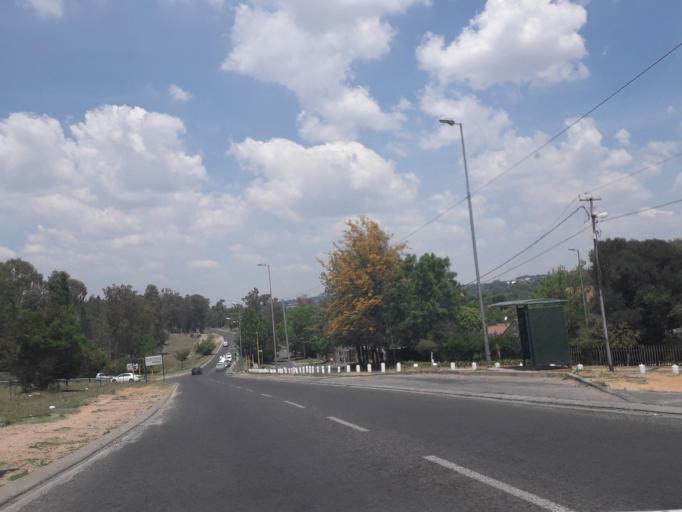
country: ZA
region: Gauteng
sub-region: City of Johannesburg Metropolitan Municipality
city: Midrand
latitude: -26.0413
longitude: 28.0697
